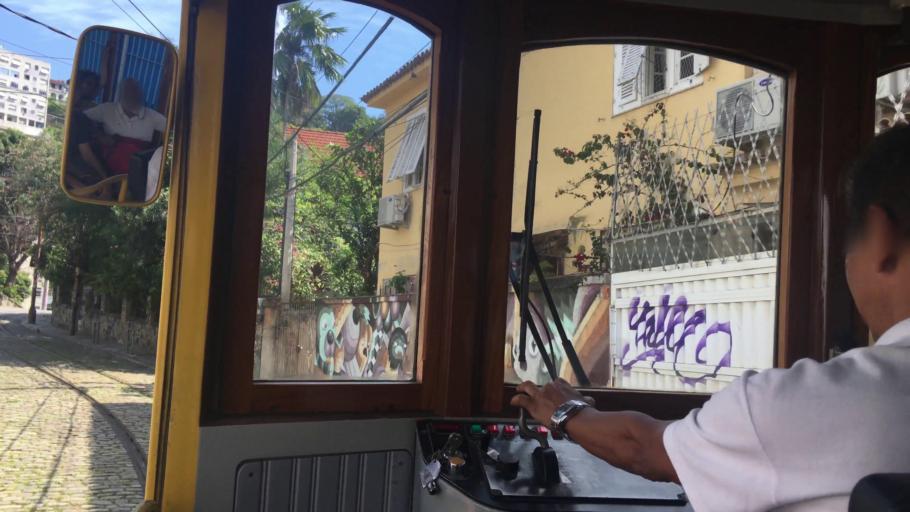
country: BR
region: Rio de Janeiro
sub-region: Rio De Janeiro
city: Rio de Janeiro
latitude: -22.9151
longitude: -43.1810
